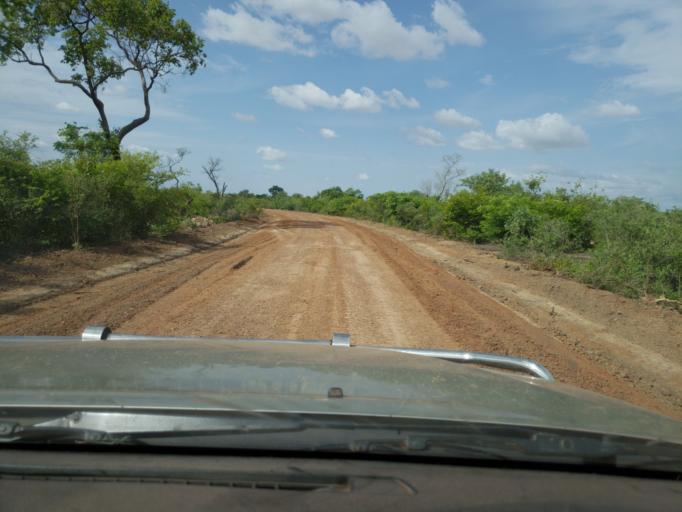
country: ML
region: Segou
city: Bla
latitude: 12.7730
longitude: -5.6140
